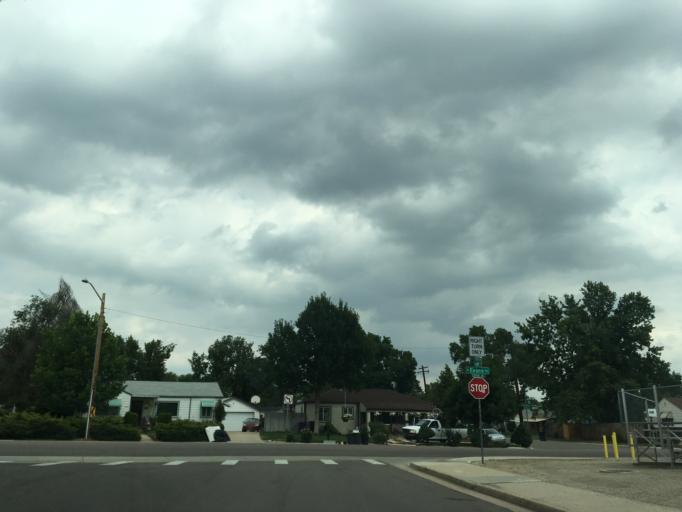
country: US
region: Colorado
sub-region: Arapahoe County
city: Sheridan
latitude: 39.6782
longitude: -105.0278
